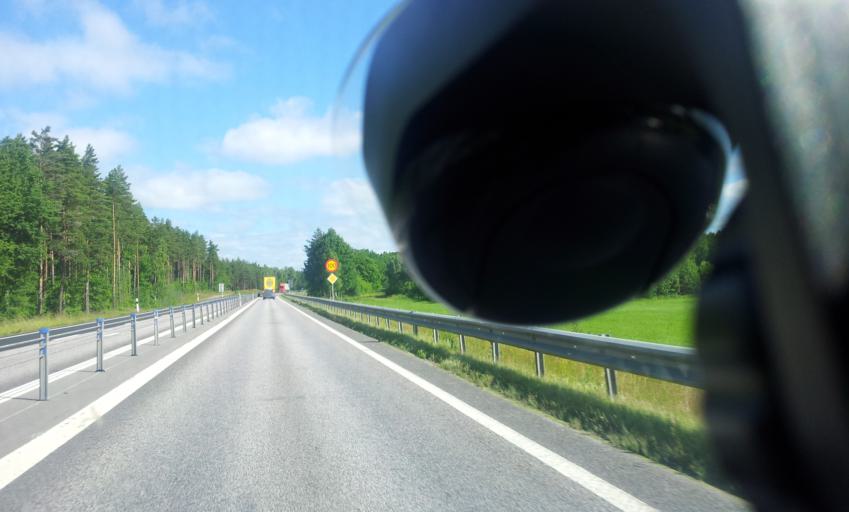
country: SE
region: Kalmar
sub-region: Kalmar Kommun
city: Lindsdal
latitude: 56.8303
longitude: 16.3670
